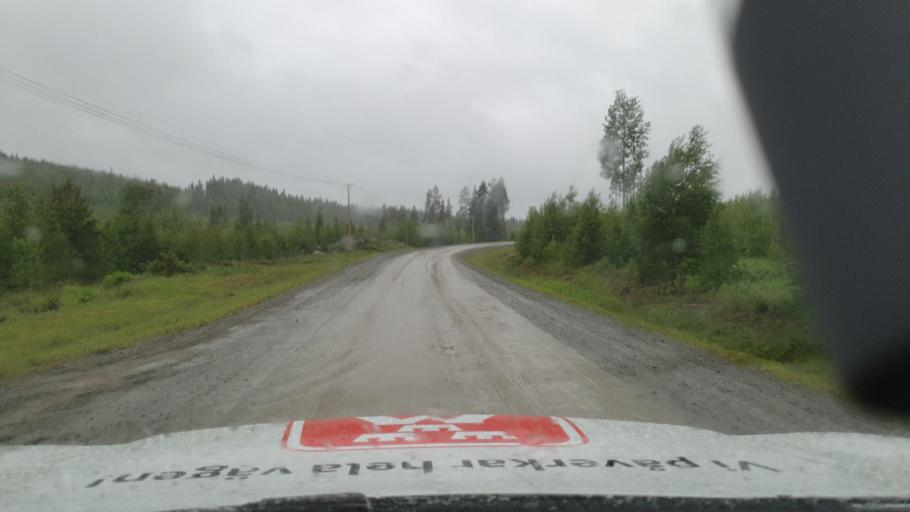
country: SE
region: Vaesterbotten
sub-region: Bjurholms Kommun
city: Bjurholm
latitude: 63.9257
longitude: 19.3681
